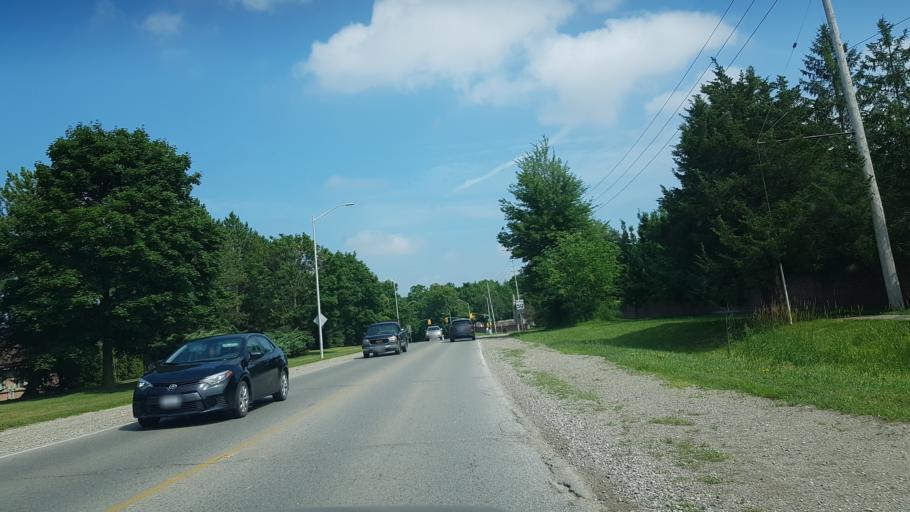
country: CA
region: Ontario
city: Delaware
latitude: 42.9648
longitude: -81.3494
